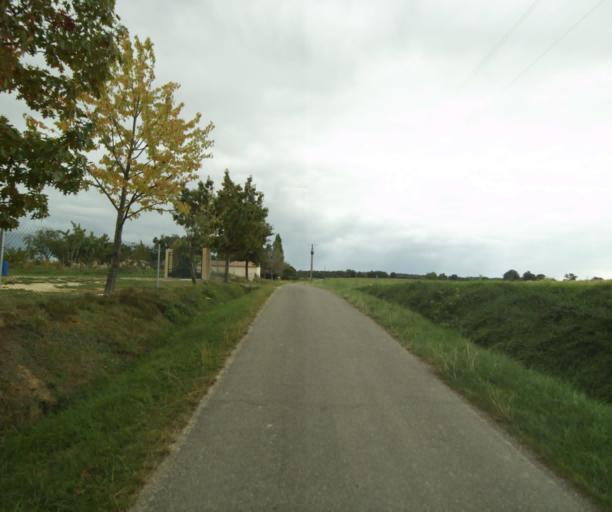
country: FR
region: Midi-Pyrenees
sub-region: Departement du Gers
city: Eauze
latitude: 43.9164
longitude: 0.1206
